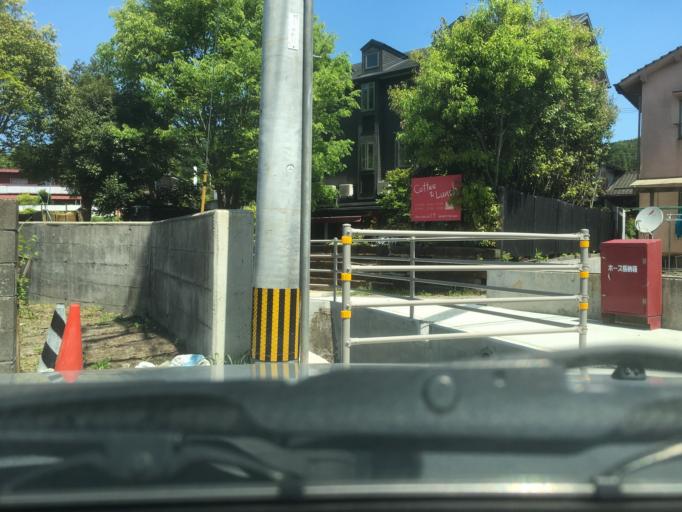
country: JP
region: Oita
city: Beppu
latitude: 33.2686
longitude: 131.3674
